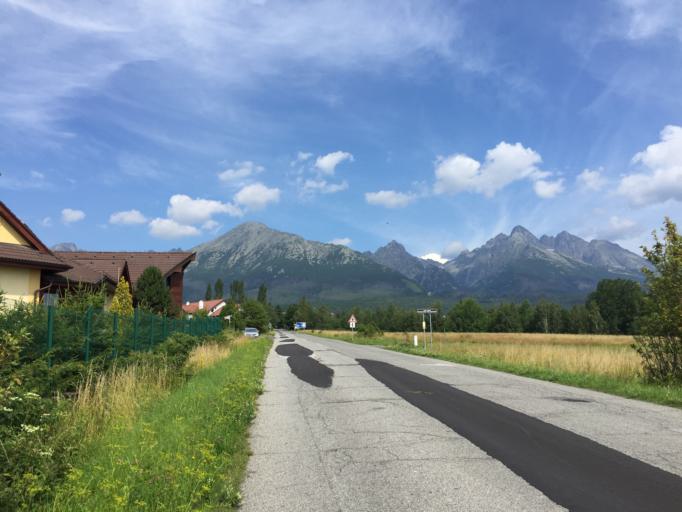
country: SK
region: Presovsky
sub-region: Okres Poprad
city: Nova Lesna
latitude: 49.1236
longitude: 20.2550
